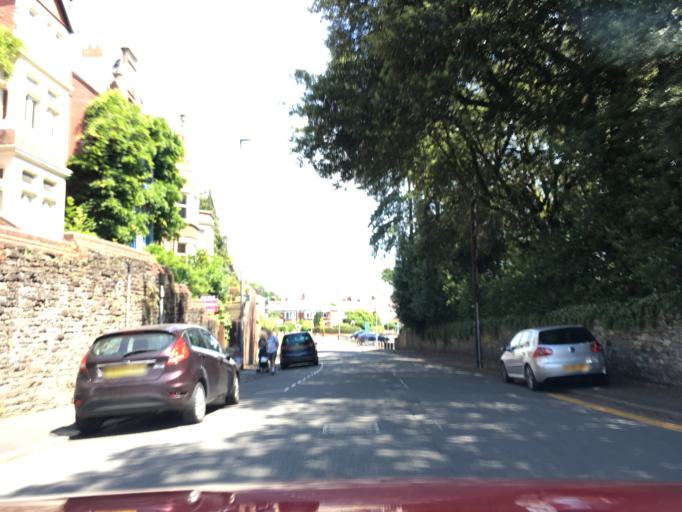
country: GB
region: Wales
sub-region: Newport
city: Newport
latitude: 51.5889
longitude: -3.0073
